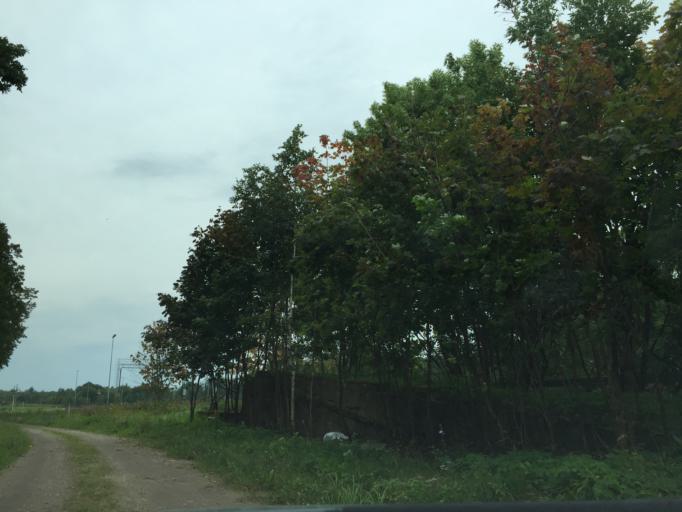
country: LV
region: Zilupes
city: Zilupe
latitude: 56.3919
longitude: 28.1107
